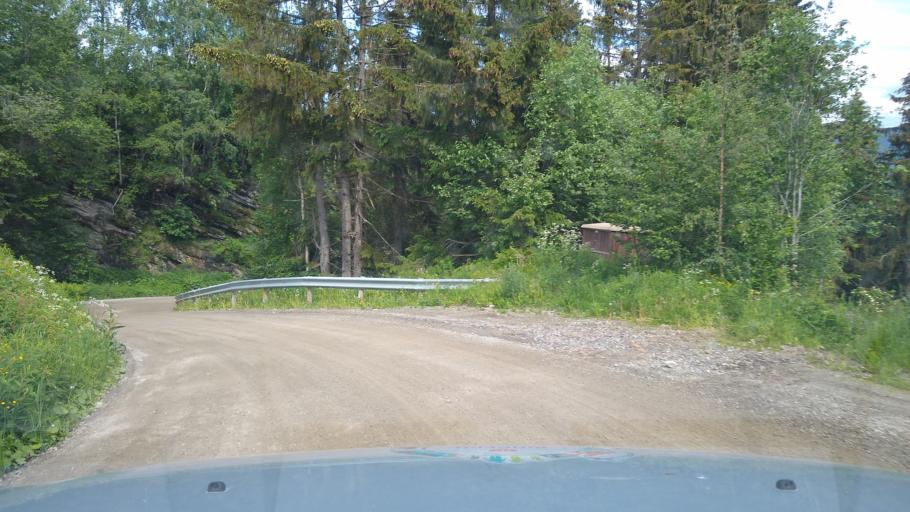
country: NO
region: Oppland
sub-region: Ringebu
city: Ringebu
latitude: 61.5159
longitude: 10.1326
